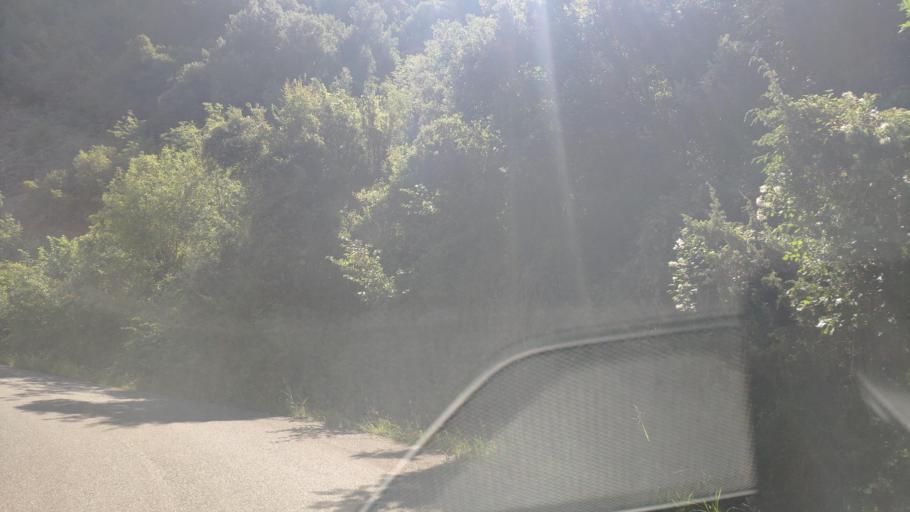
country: GR
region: Central Greece
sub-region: Nomos Evrytanias
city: Kerasochori
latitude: 39.0033
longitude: 21.5870
